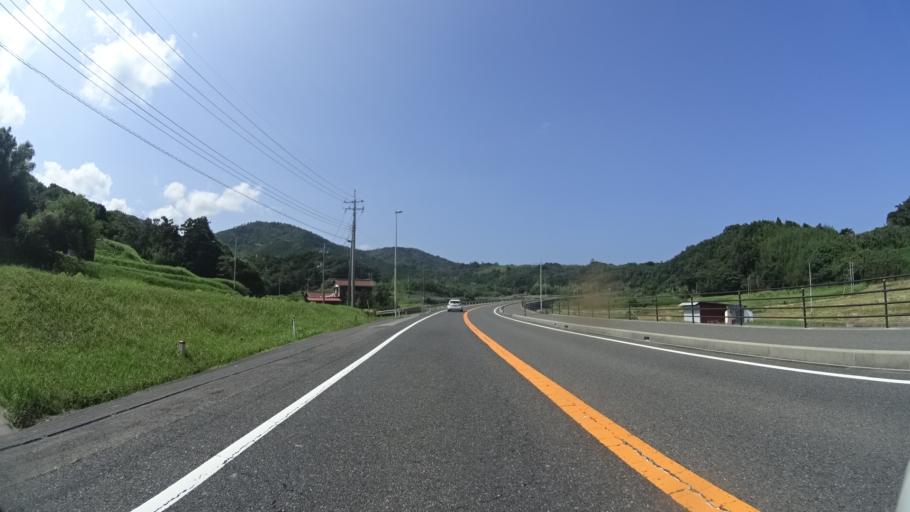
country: JP
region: Shimane
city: Masuda
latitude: 34.6710
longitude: 131.7335
